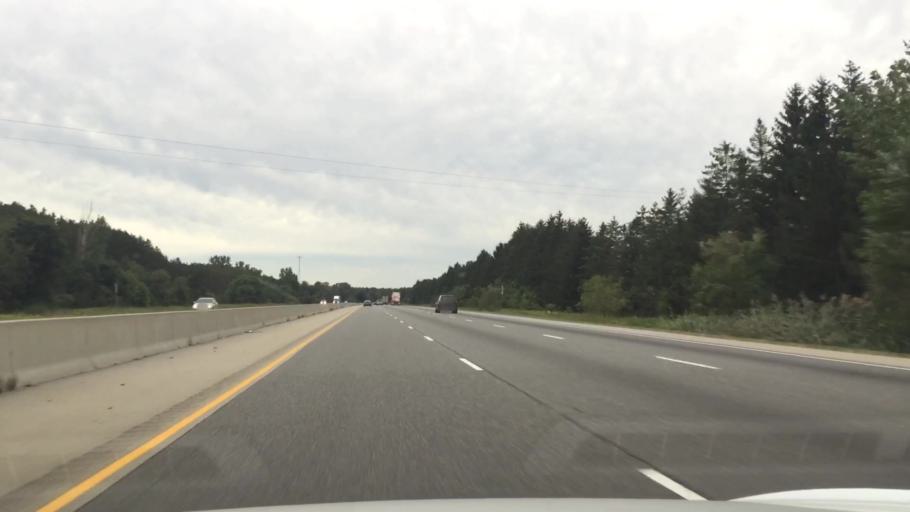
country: CA
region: Ontario
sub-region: Oxford County
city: Woodstock
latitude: 43.1847
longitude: -80.6437
